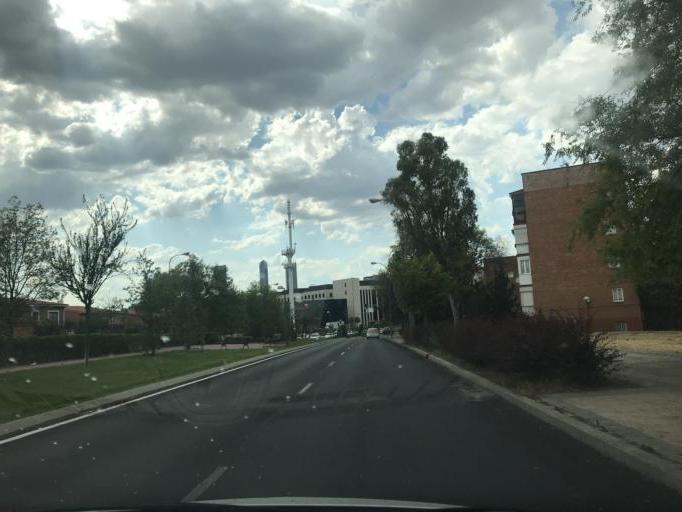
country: ES
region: Madrid
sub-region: Provincia de Madrid
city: Pinar de Chamartin
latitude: 40.4722
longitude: -3.6611
